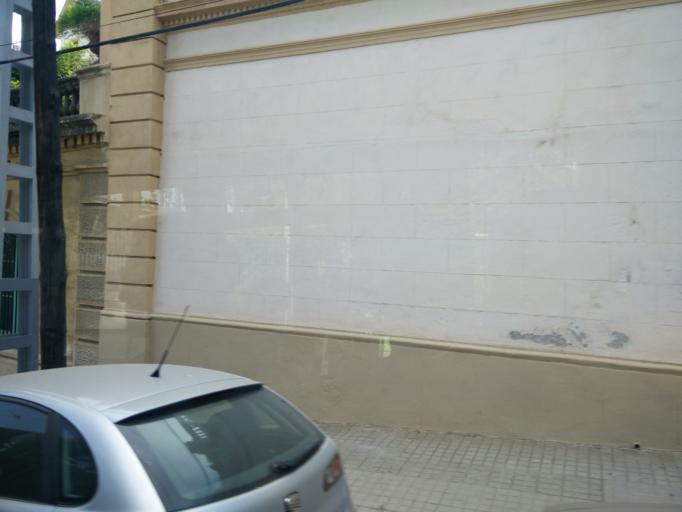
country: ES
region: Catalonia
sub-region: Provincia de Barcelona
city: Sarria-Sant Gervasi
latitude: 41.4160
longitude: 2.1298
